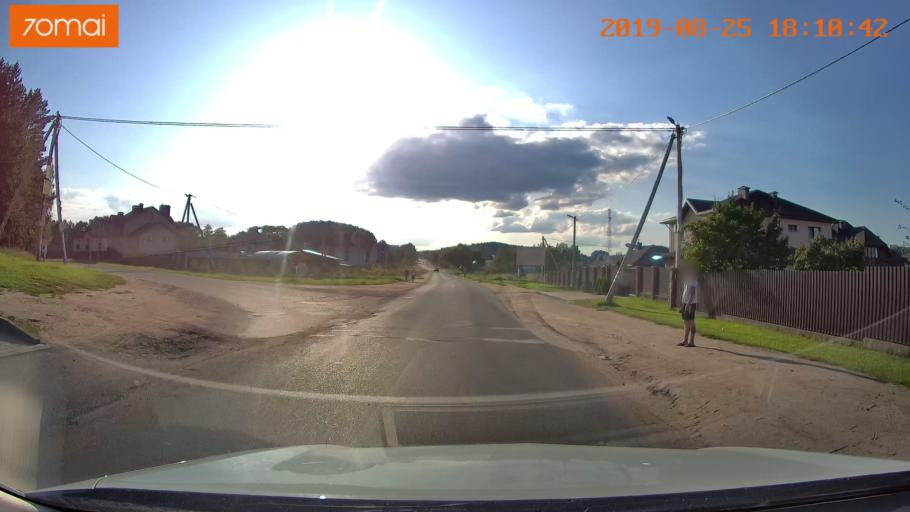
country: BY
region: Minsk
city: Khatsyezhyna
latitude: 53.9397
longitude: 27.3269
